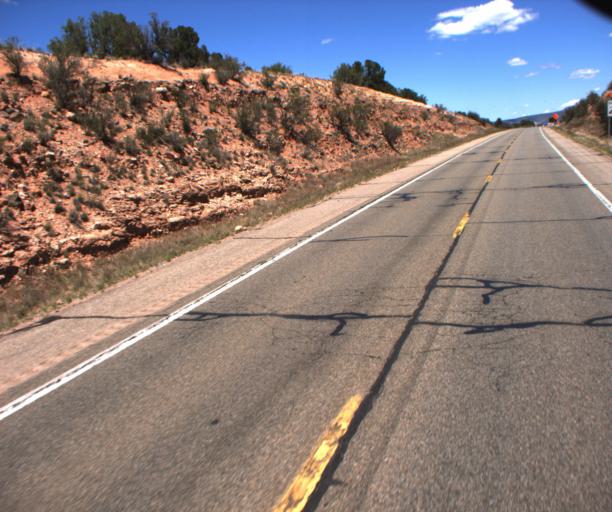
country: US
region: Arizona
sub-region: Yavapai County
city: Paulden
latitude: 34.9804
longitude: -112.4014
